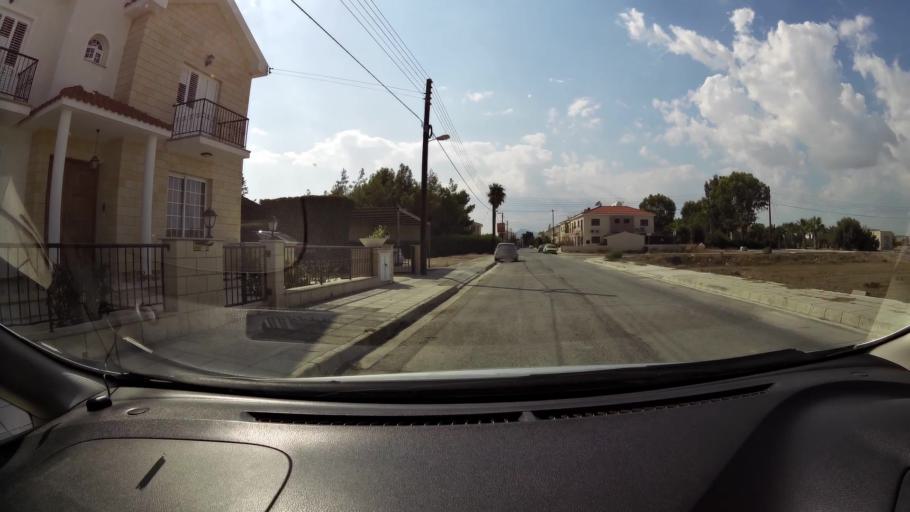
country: CY
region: Larnaka
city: Dhromolaxia
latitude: 34.9074
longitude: 33.5899
